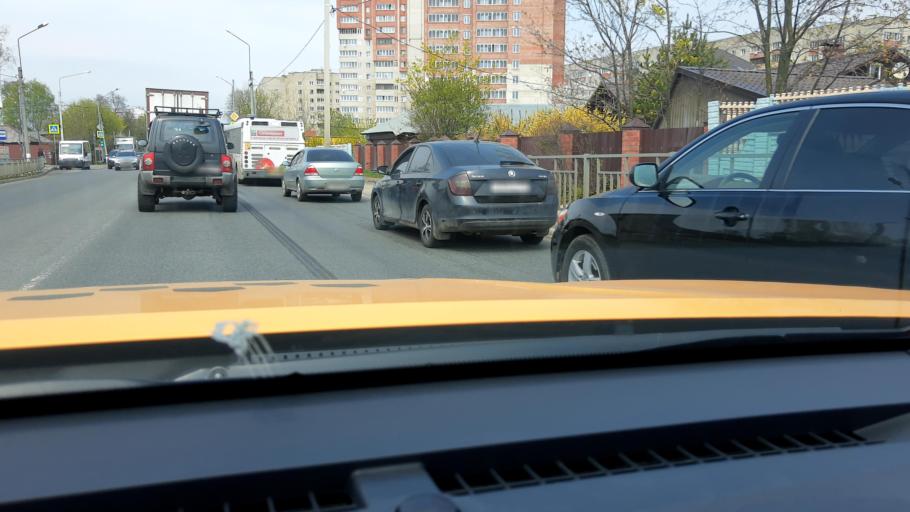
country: RU
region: Moskovskaya
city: Noginsk
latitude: 55.8727
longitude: 38.4350
